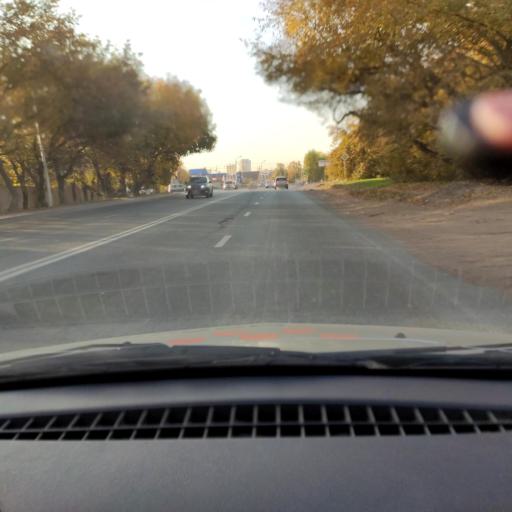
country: RU
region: Bashkortostan
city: Ufa
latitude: 54.7821
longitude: 56.0528
